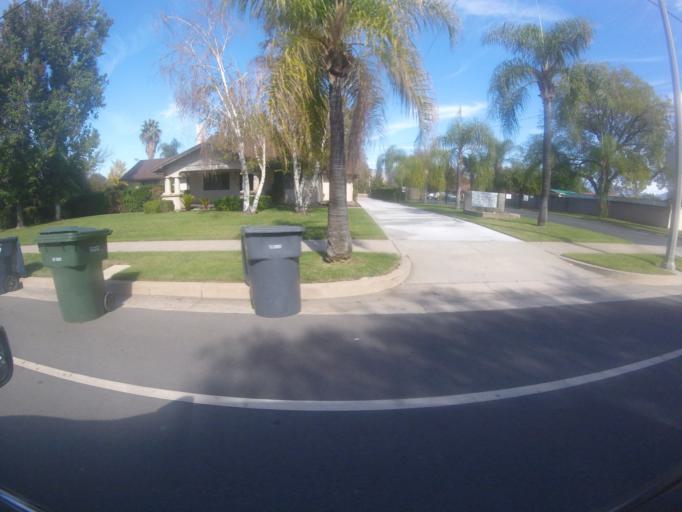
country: US
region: California
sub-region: San Bernardino County
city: Mentone
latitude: 34.0664
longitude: -117.1593
